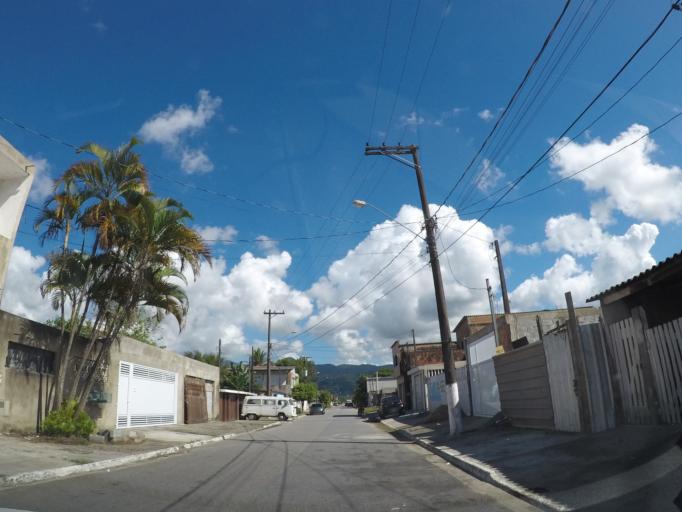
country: BR
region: Sao Paulo
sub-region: Praia Grande
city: Praia Grande
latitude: -24.0236
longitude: -46.5064
